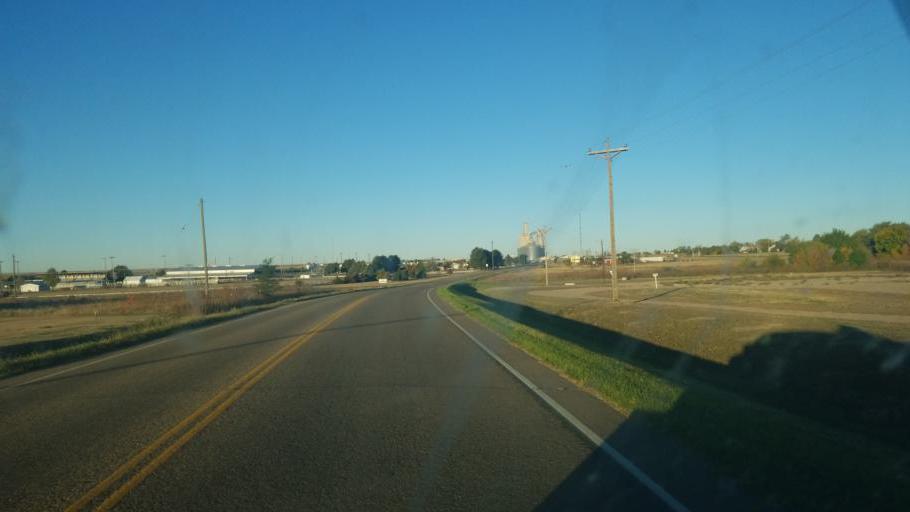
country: US
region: Colorado
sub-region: Cheyenne County
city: Cheyenne Wells
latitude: 38.8166
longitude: -102.3486
